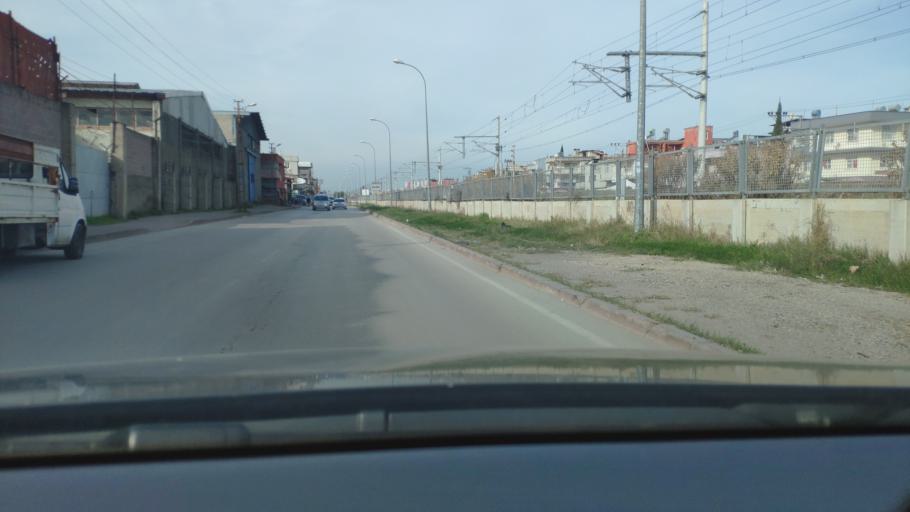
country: TR
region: Adana
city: Seyhan
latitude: 36.9975
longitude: 35.2723
